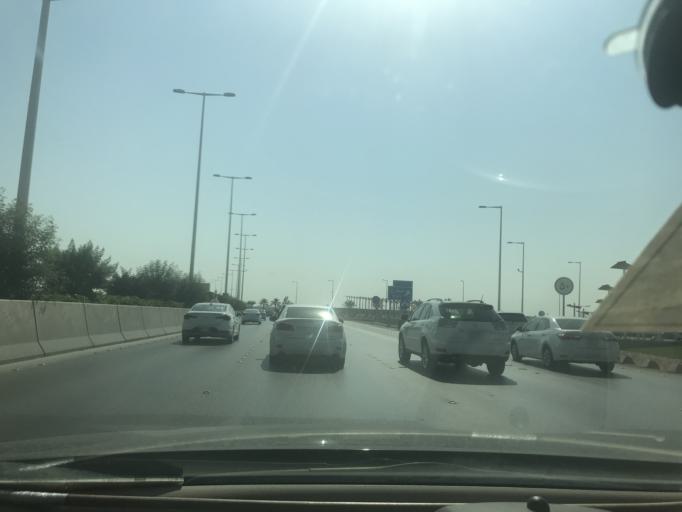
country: SA
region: Ar Riyad
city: Riyadh
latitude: 24.7261
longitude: 46.7099
